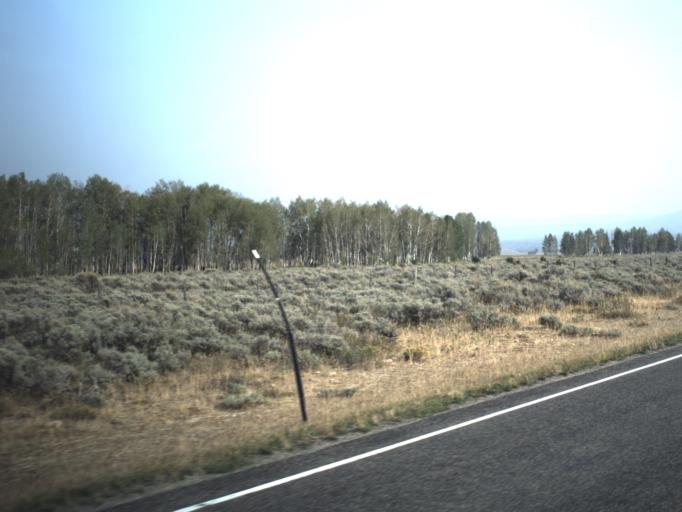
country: US
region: Wyoming
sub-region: Uinta County
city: Evanston
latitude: 40.9704
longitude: -110.8493
